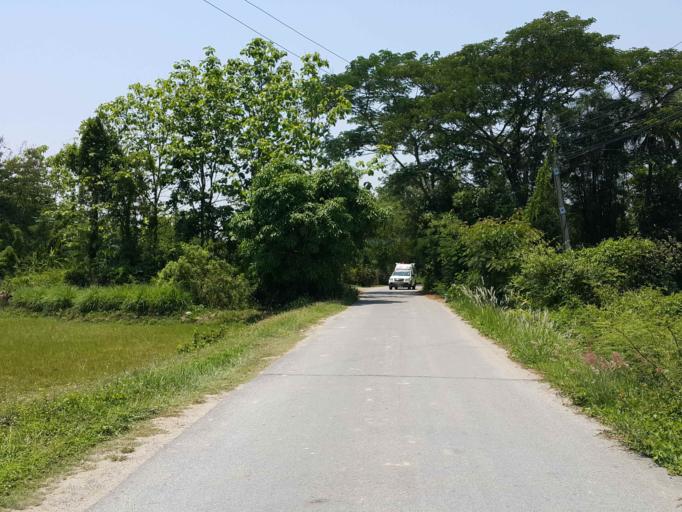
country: TH
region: Chiang Mai
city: San Sai
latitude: 18.8290
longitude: 99.1025
